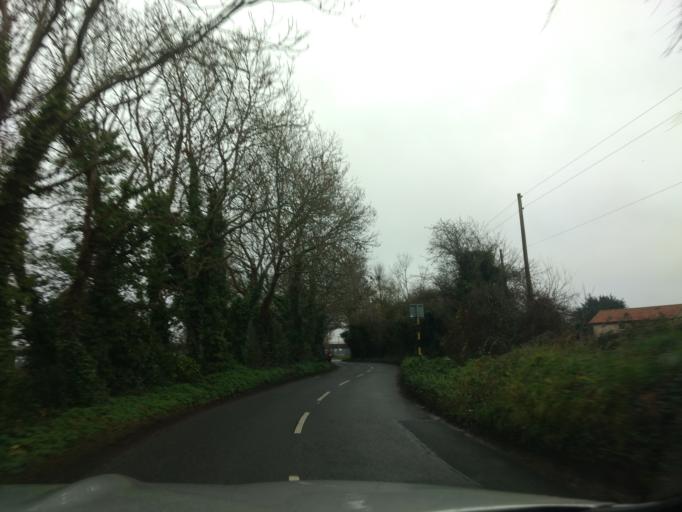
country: IE
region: Leinster
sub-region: Fingal County
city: Swords
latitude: 53.4673
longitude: -6.2080
